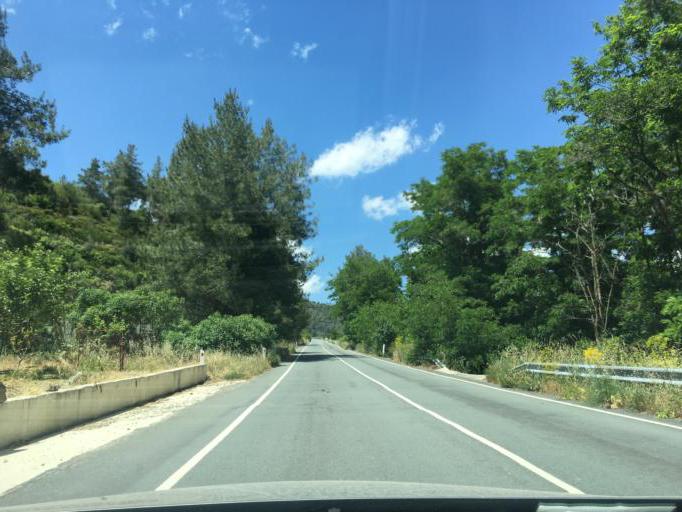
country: CY
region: Limassol
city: Pelendri
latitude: 34.9065
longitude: 32.9431
